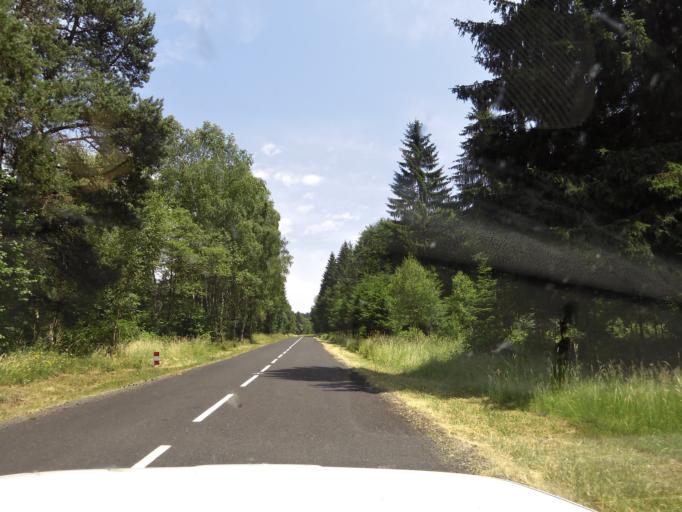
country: FR
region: Auvergne
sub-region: Departement du Puy-de-Dome
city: Orcines
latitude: 45.7636
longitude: 2.9404
